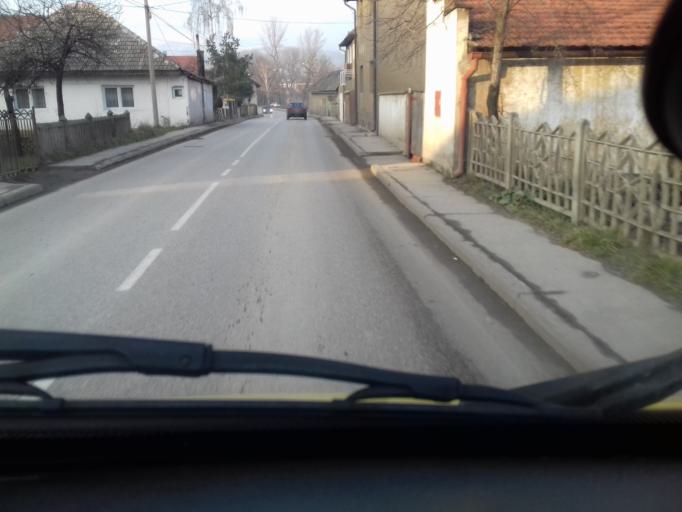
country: BA
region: Federation of Bosnia and Herzegovina
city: Kakanj
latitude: 44.1165
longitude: 18.1166
